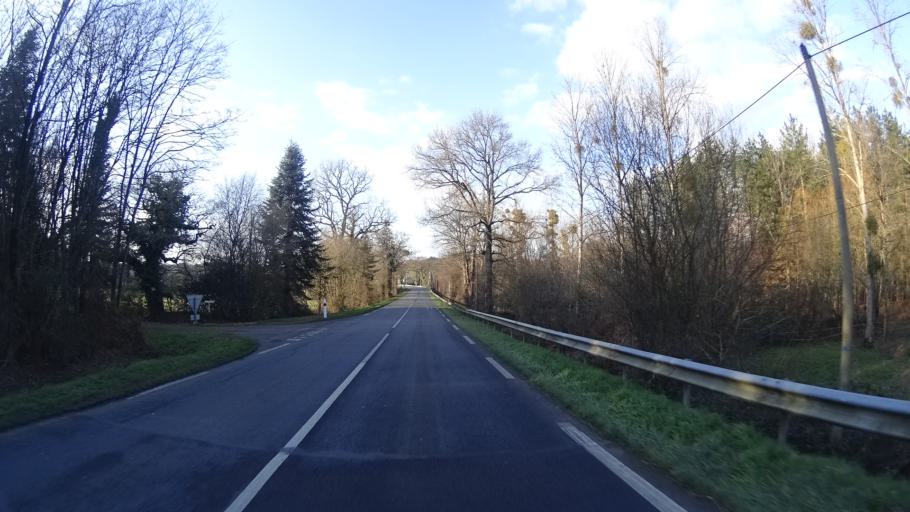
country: FR
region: Pays de la Loire
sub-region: Departement de la Loire-Atlantique
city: Fegreac
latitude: 47.5981
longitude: -2.0141
